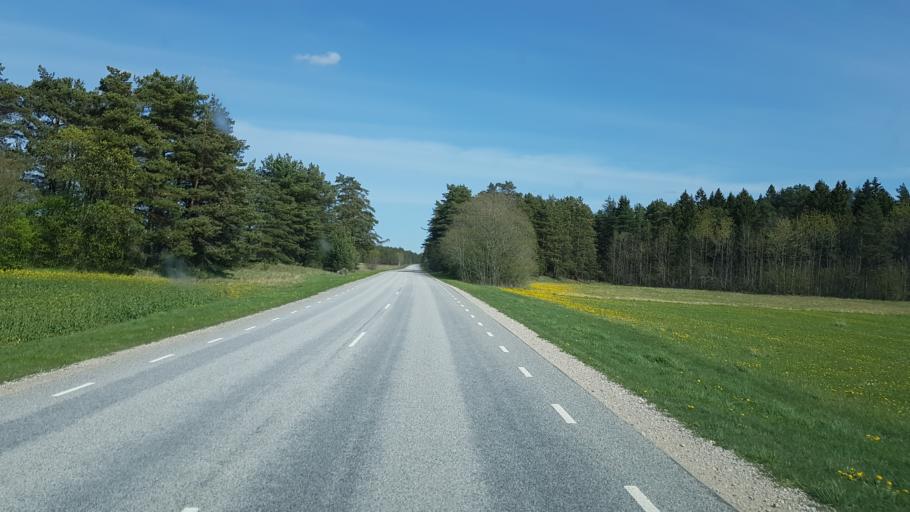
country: EE
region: Harju
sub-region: Paldiski linn
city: Paldiski
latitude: 59.2172
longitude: 24.0530
